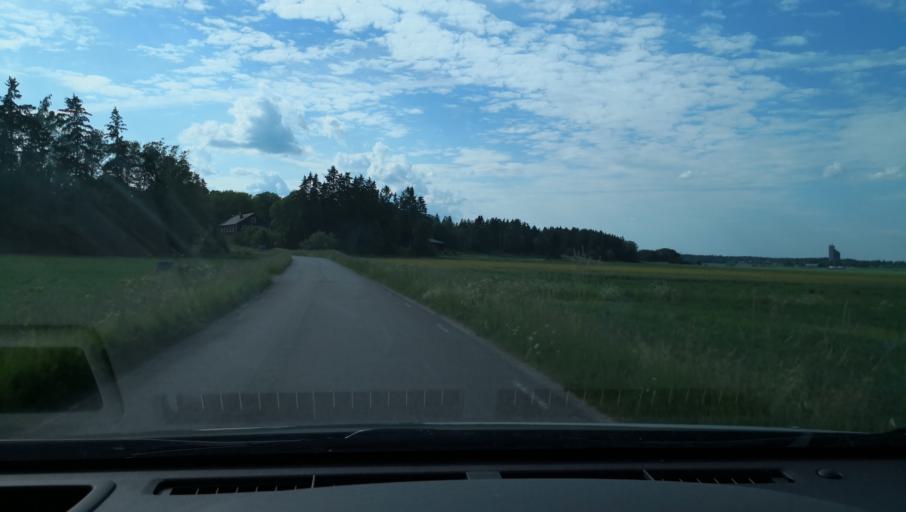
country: SE
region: Uppsala
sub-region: Enkopings Kommun
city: Irsta
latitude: 59.7532
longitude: 16.9544
